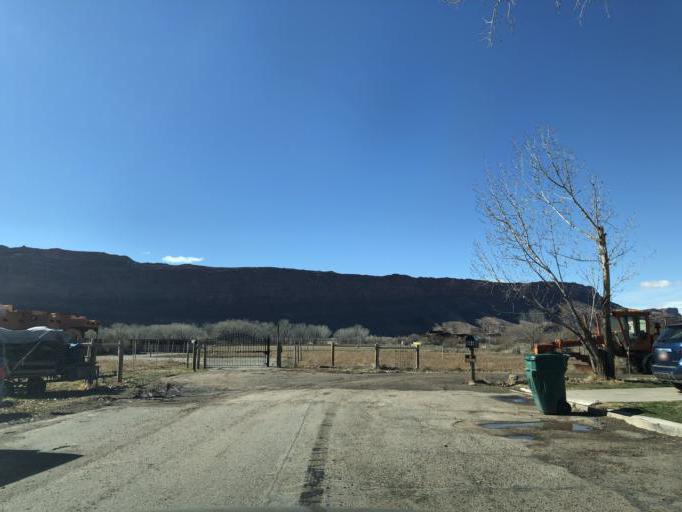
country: US
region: Utah
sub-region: Grand County
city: Moab
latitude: 38.5877
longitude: -109.5654
